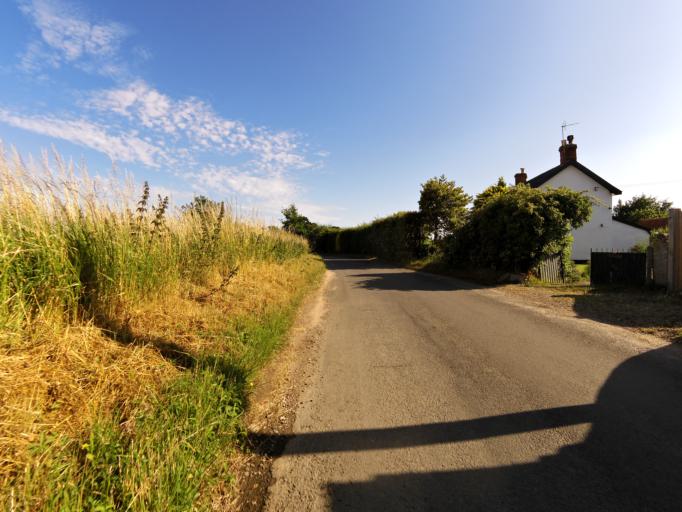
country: GB
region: England
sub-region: Suffolk
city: Leiston
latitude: 52.2706
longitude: 1.5679
